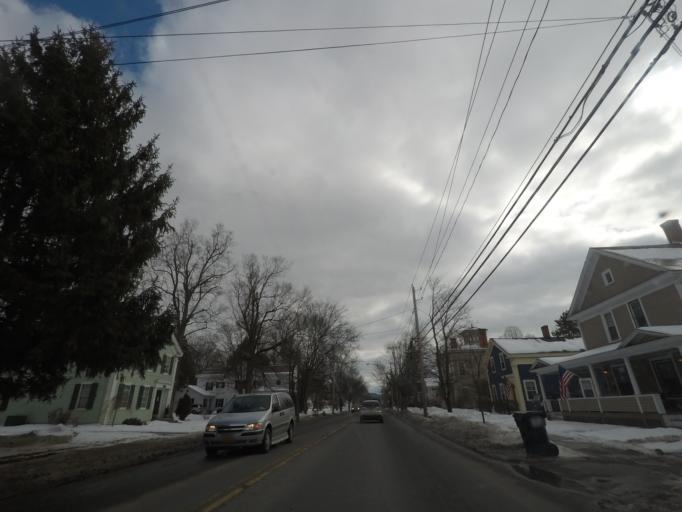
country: US
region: New York
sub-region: Washington County
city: Greenwich
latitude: 43.0932
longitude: -73.5040
